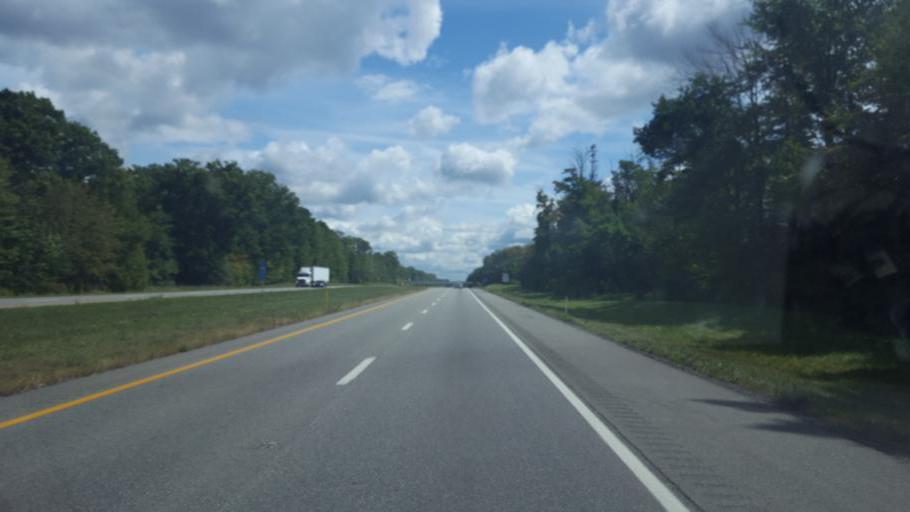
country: US
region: Ohio
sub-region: Geauga County
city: Bainbridge
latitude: 41.3864
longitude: -81.3306
